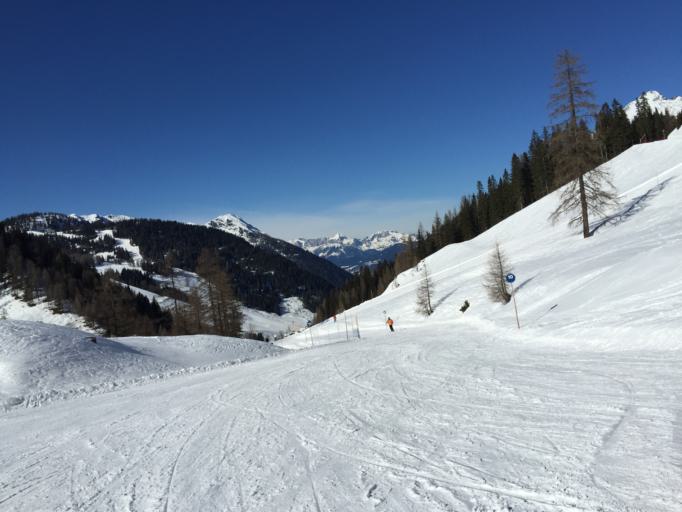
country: AT
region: Salzburg
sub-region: Politischer Bezirk Sankt Johann im Pongau
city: Untertauern
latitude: 47.2813
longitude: 13.4649
